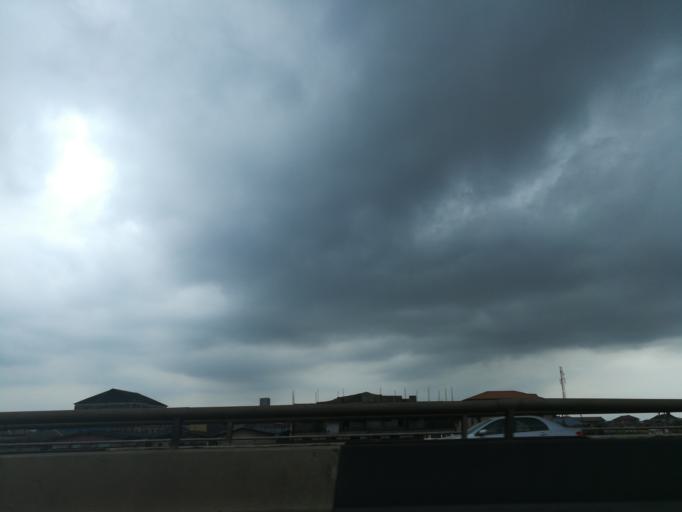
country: NG
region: Lagos
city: Somolu
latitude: 6.5409
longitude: 3.3996
